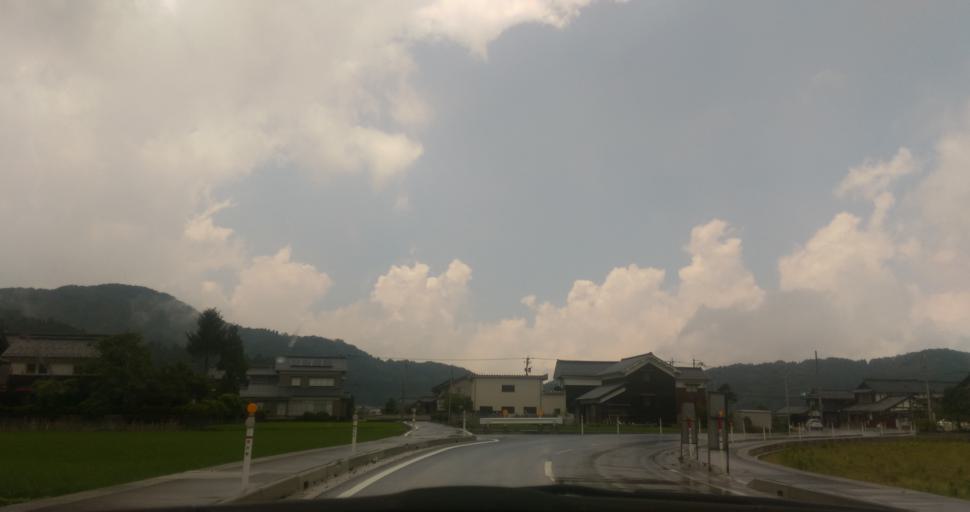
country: JP
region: Fukui
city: Fukui-shi
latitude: 36.0144
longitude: 136.2029
